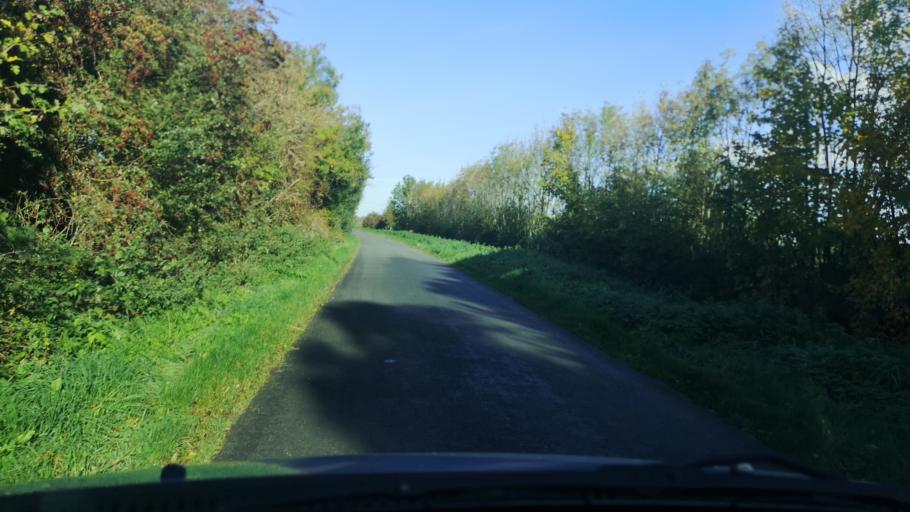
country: GB
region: England
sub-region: Doncaster
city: Askern
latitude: 53.6200
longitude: -1.1330
